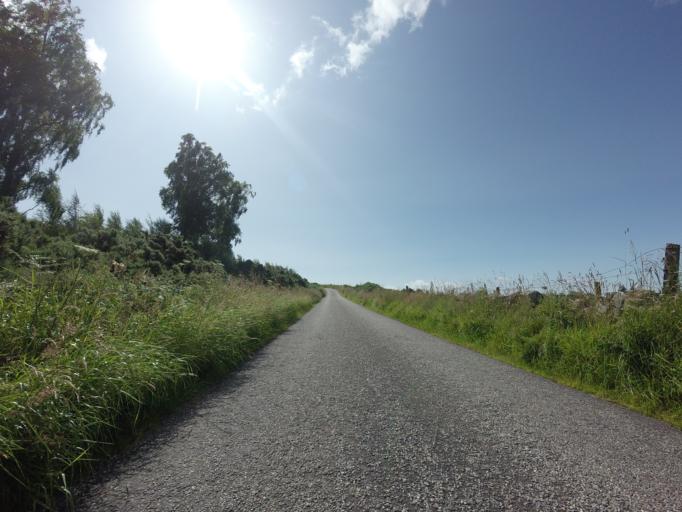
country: GB
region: Scotland
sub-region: Highland
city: Nairn
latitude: 57.5326
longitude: -3.8645
